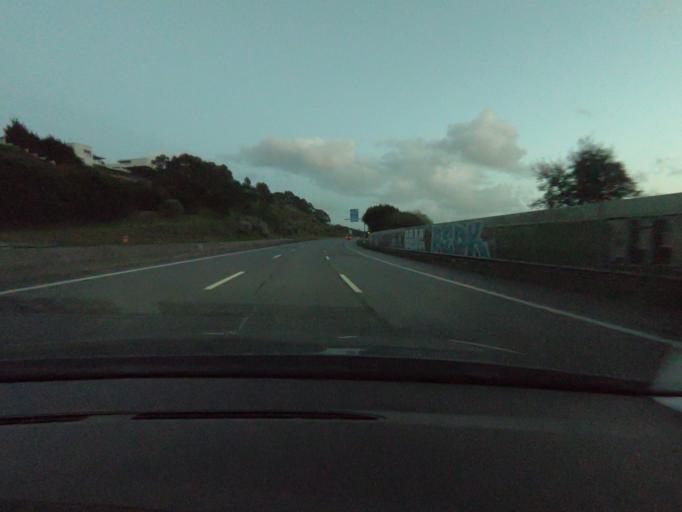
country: PT
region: Lisbon
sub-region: Oeiras
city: Barcarena
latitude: 38.7322
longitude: -9.2749
